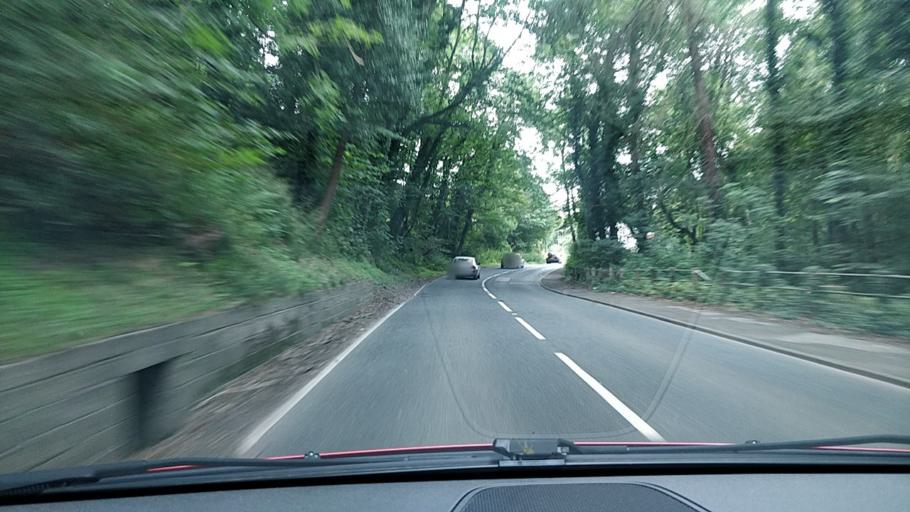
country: GB
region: Wales
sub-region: County of Flintshire
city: Leeswood
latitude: 53.1326
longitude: -3.0822
